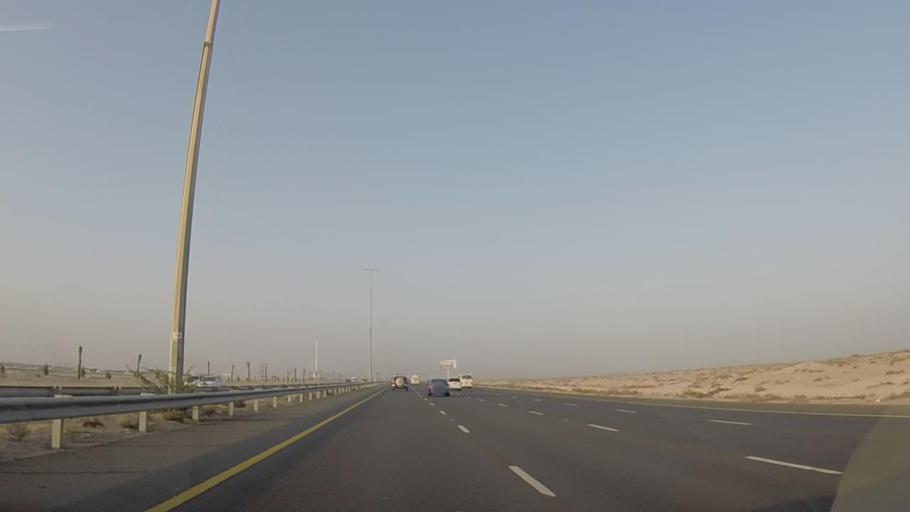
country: AE
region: Dubai
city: Dubai
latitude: 24.9309
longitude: 55.0156
